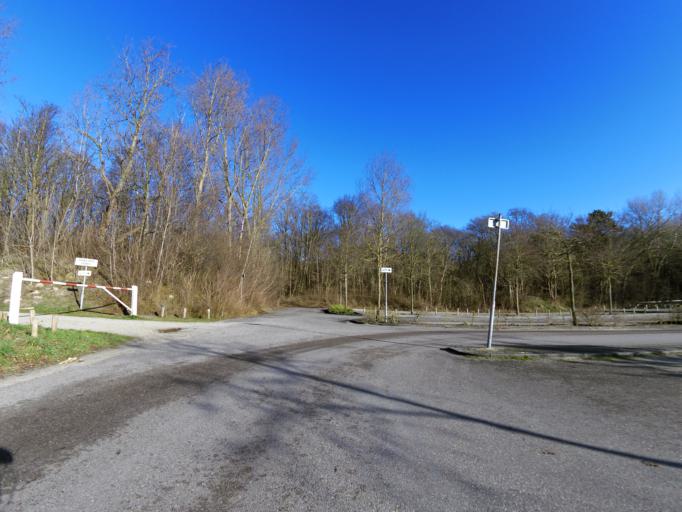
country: NL
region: South Holland
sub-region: Gemeente Hellevoetsluis
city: Nieuw-Helvoet
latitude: 51.8710
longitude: 4.0541
